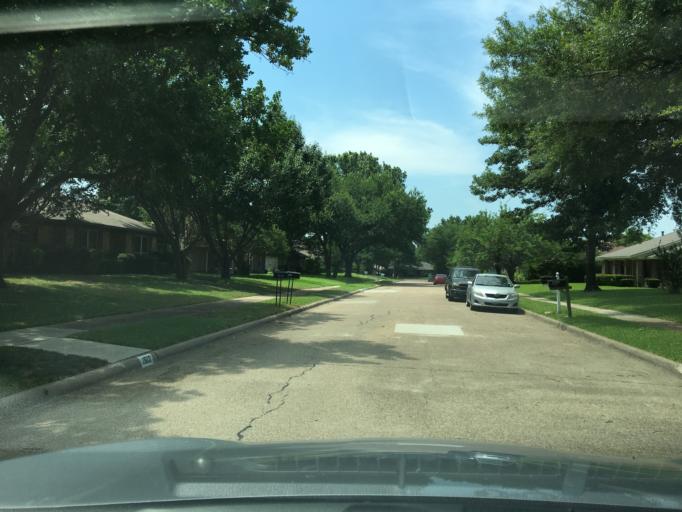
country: US
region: Texas
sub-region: Dallas County
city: Richardson
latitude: 32.9678
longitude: -96.6971
